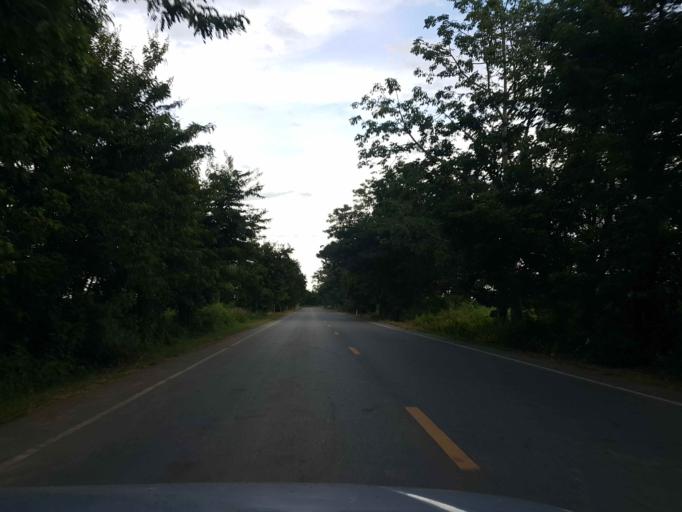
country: TH
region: Sukhothai
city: Sawankhalok
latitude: 17.3755
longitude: 99.7394
